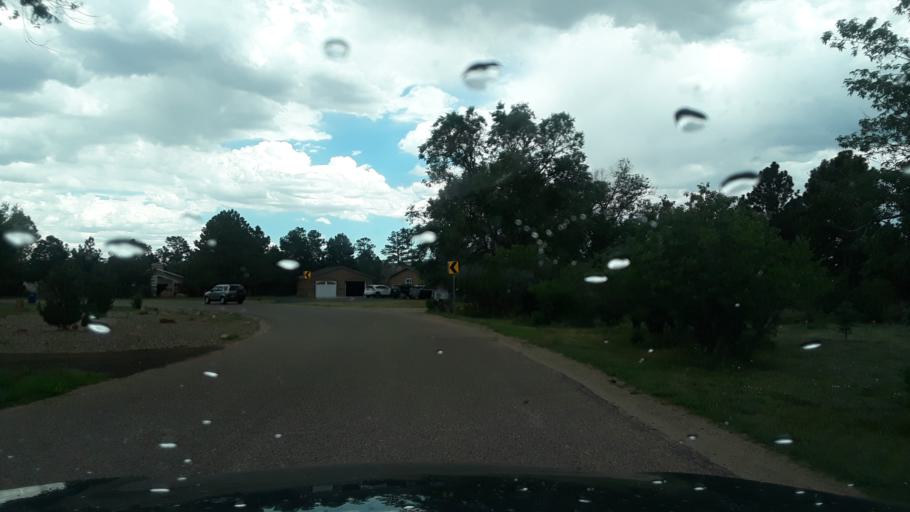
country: US
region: Colorado
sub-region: El Paso County
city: Air Force Academy
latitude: 38.9399
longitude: -104.8170
